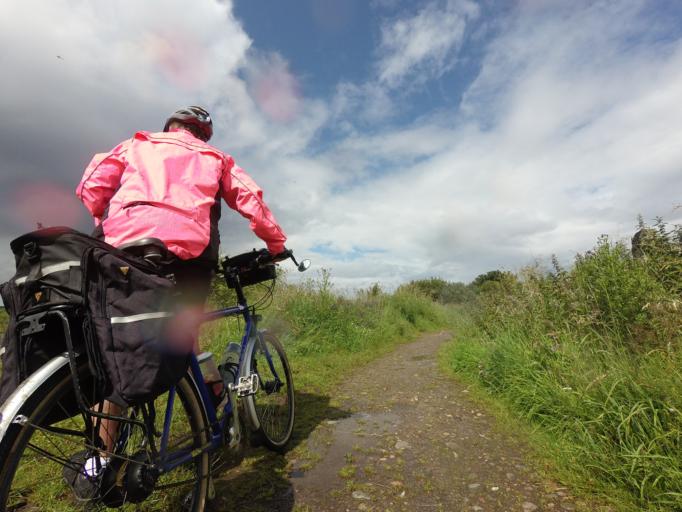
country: GB
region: Scotland
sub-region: Moray
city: Fochabers
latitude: 57.6710
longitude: -3.0923
